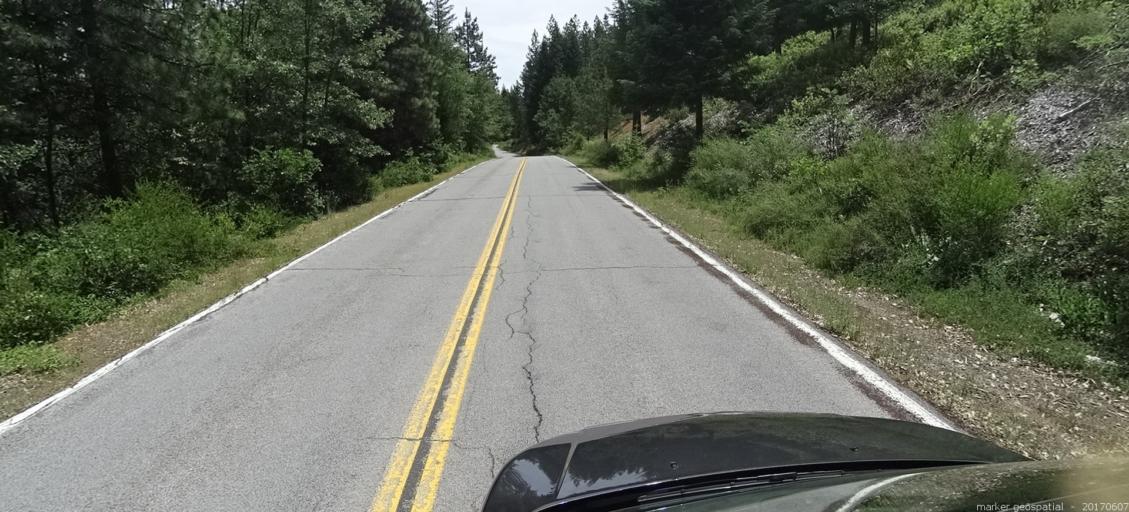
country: US
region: California
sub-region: Siskiyou County
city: Mount Shasta
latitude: 41.2874
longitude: -122.3654
